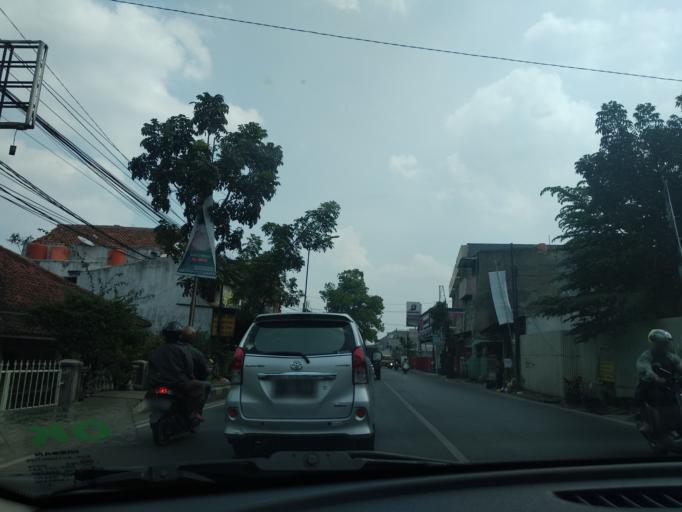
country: ID
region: West Java
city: Cimahi
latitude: -6.8688
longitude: 107.5311
